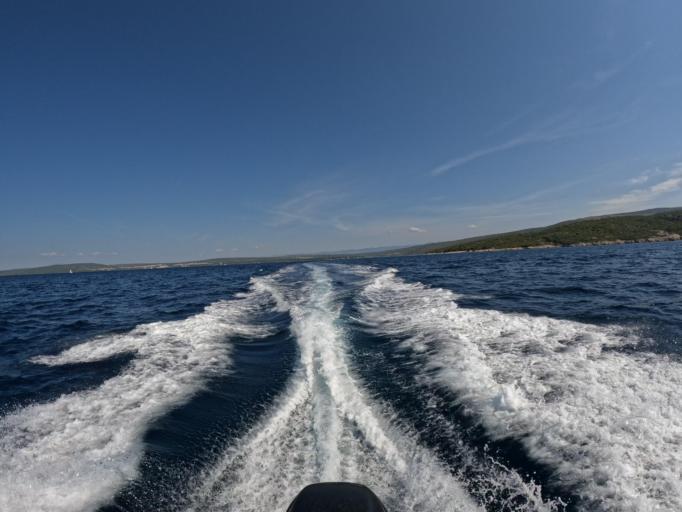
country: HR
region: Primorsko-Goranska
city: Punat
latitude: 44.9738
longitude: 14.6089
